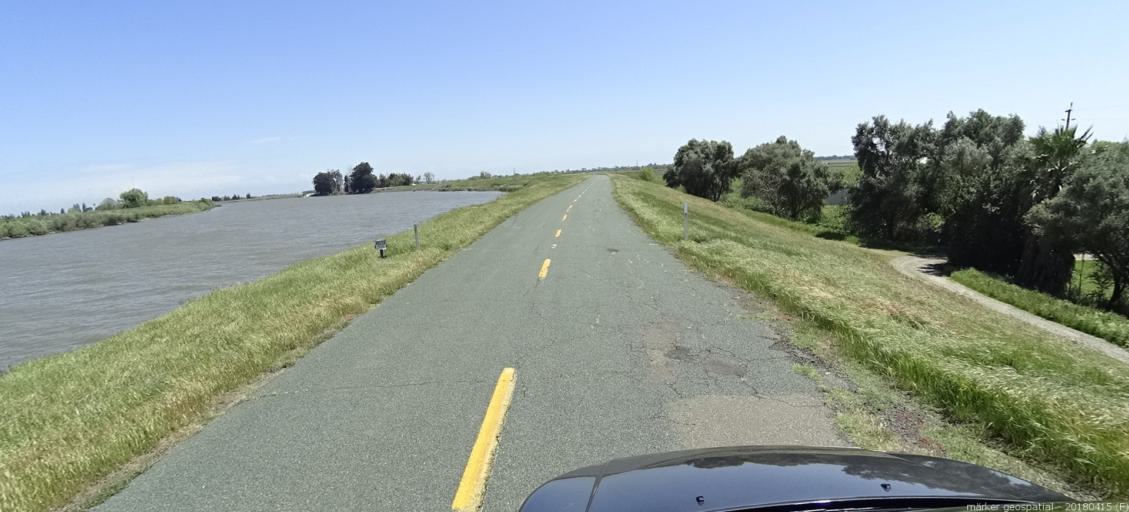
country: US
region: California
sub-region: Solano County
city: Rio Vista
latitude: 38.1928
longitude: -121.6279
